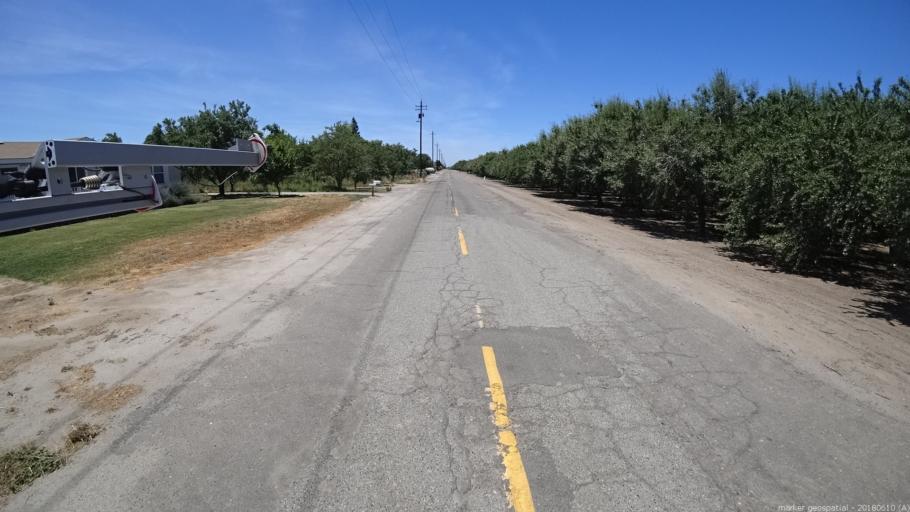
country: US
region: California
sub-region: Madera County
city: Chowchilla
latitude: 37.0545
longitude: -120.2904
